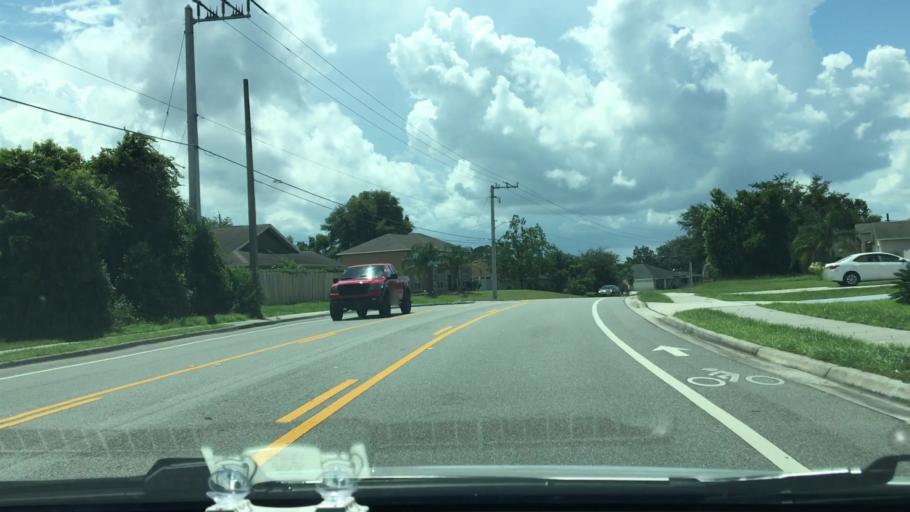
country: US
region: Florida
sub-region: Volusia County
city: Deltona
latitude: 28.8894
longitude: -81.2139
